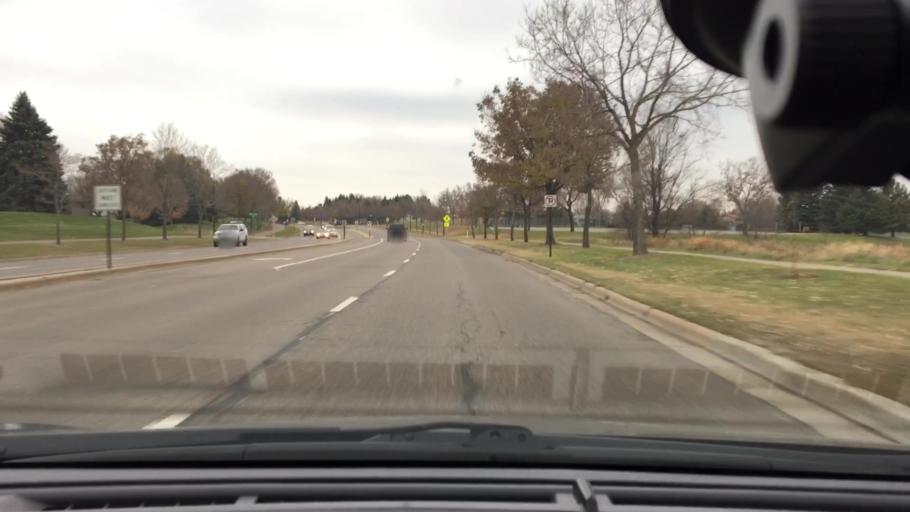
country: US
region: Minnesota
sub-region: Hennepin County
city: Osseo
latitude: 45.1205
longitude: -93.4500
